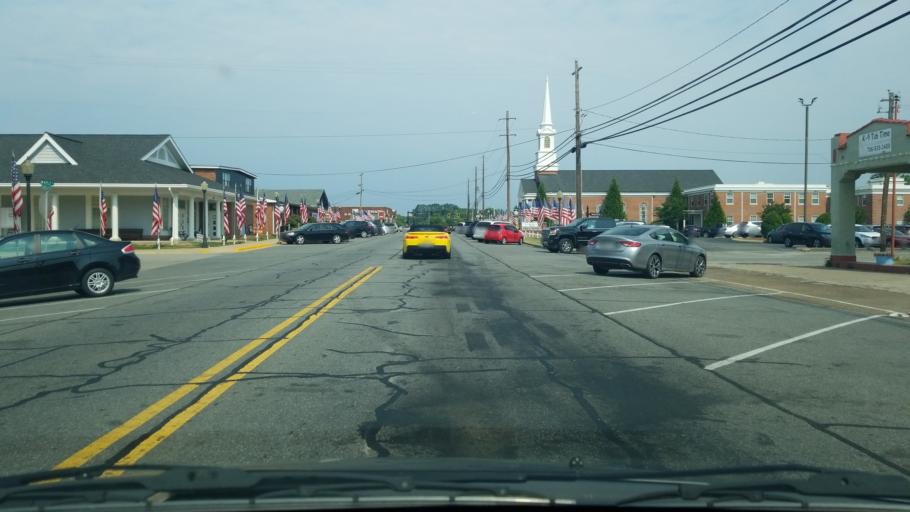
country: US
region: Georgia
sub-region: Catoosa County
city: Ringgold
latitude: 34.9162
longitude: -85.1108
